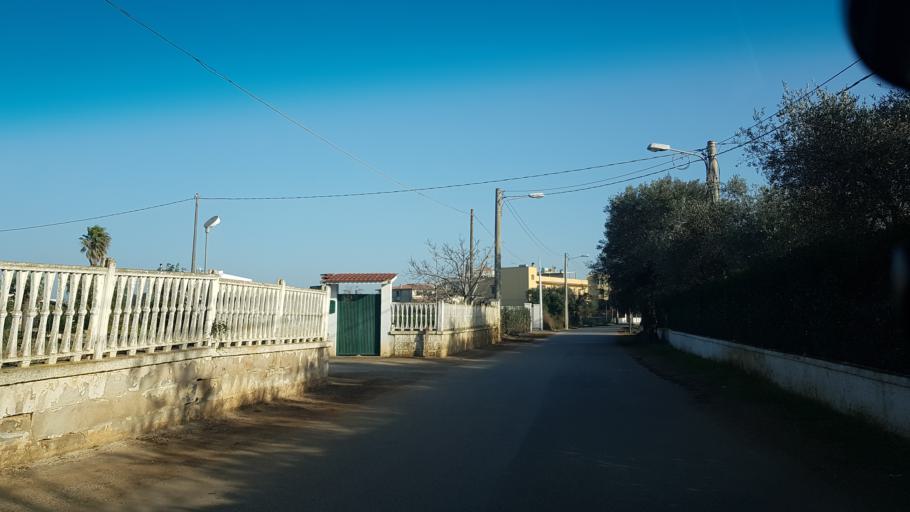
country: IT
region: Apulia
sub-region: Provincia di Brindisi
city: San Vito dei Normanni
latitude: 40.6653
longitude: 17.6918
